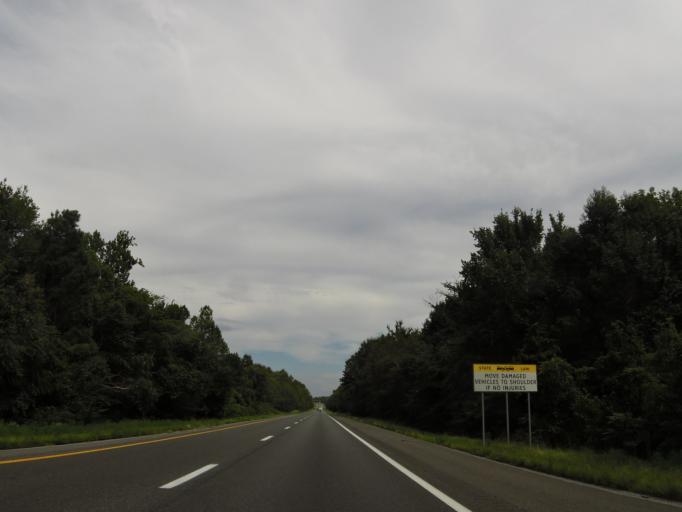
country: US
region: Kentucky
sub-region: Livingston County
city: Ledbetter
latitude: 36.9926
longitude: -88.4484
